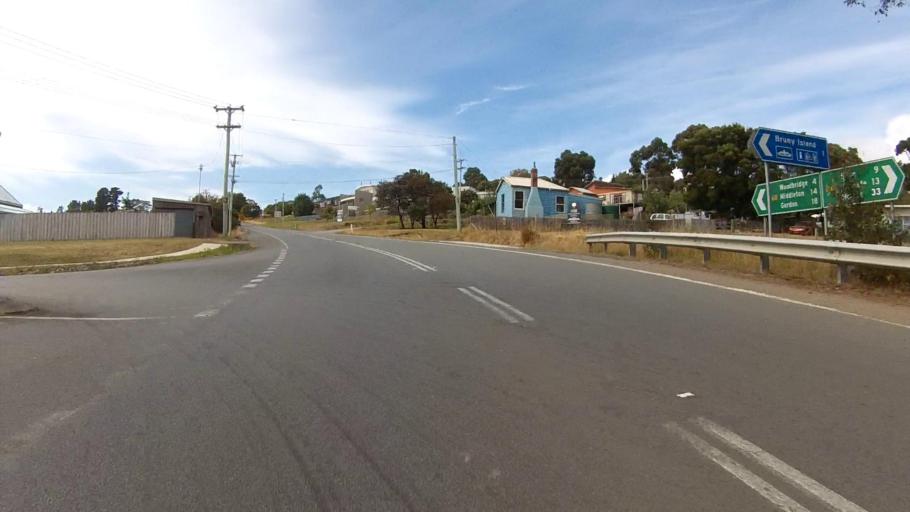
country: AU
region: Tasmania
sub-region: Kingborough
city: Kettering
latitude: -43.1281
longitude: 147.2465
